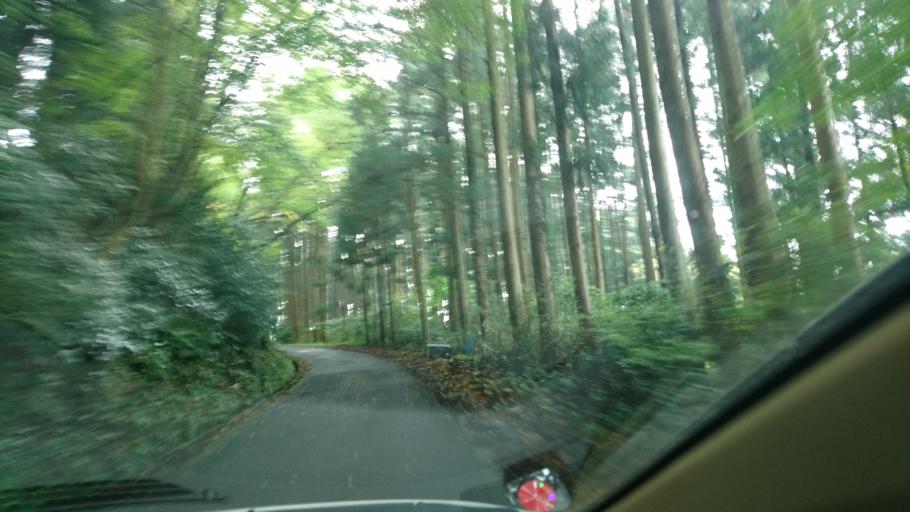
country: JP
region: Iwate
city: Ichinoseki
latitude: 38.9584
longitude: 141.1866
